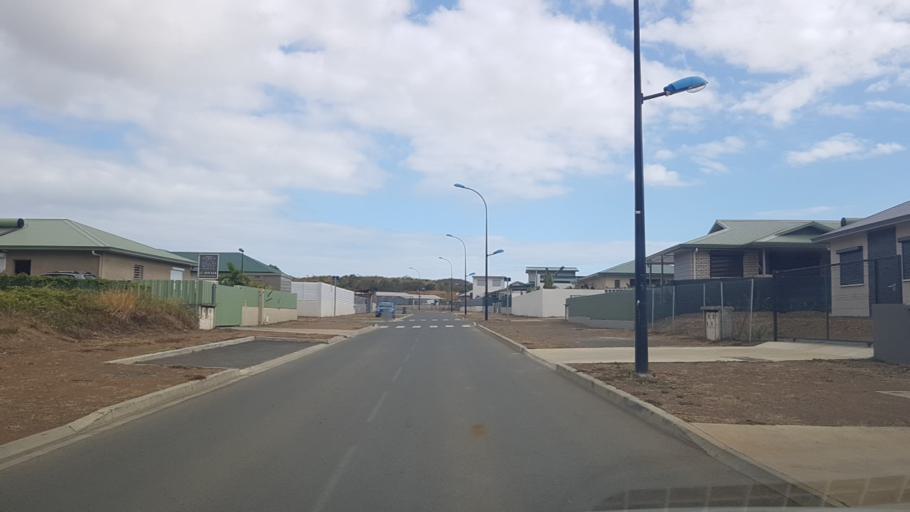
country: NC
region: South Province
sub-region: Dumbea
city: Dumbea
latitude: -22.2007
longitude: 166.4418
